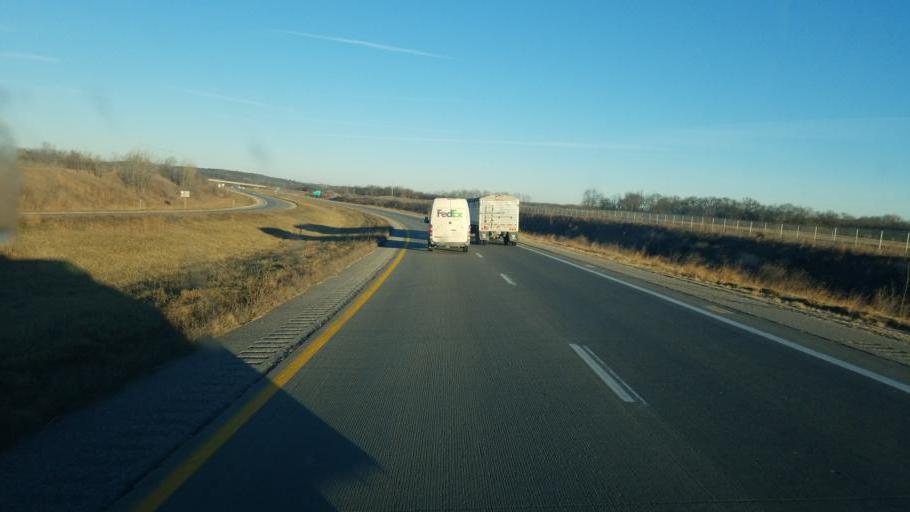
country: US
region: Iowa
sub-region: Wapello County
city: Eddyville
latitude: 41.1658
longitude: -92.6243
